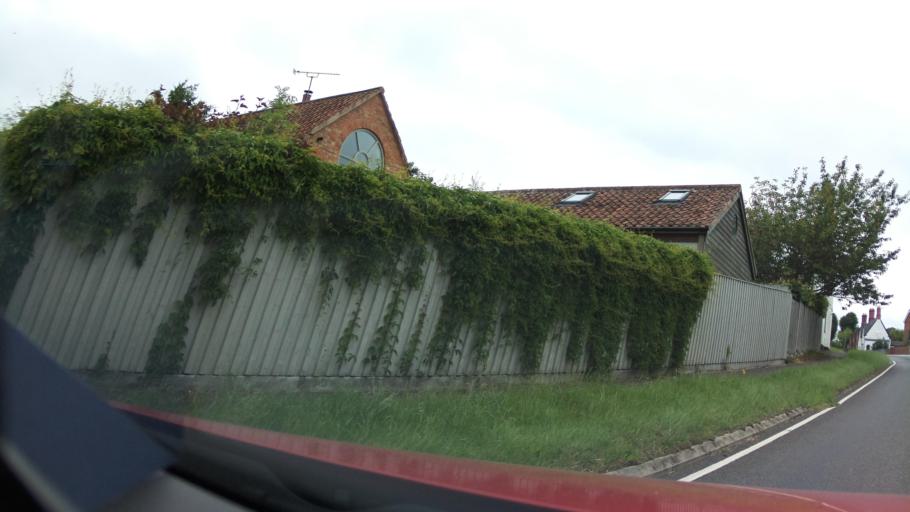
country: GB
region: England
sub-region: Leicestershire
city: Melton Mowbray
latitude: 52.7425
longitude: -0.8626
